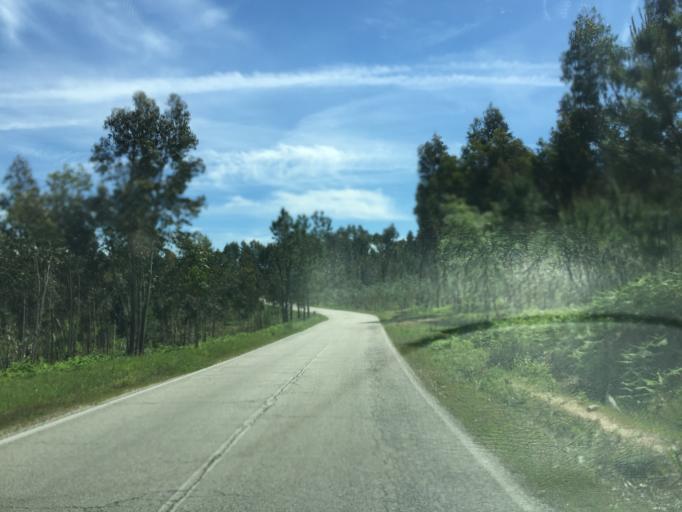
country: PT
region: Coimbra
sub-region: Soure
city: Soure
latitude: 40.0551
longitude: -8.6799
